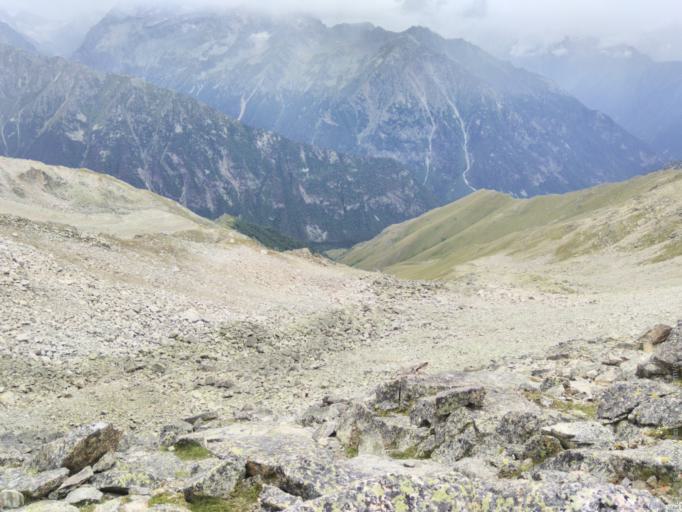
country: RU
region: Karachayevo-Cherkesiya
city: Uchkulan
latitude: 43.3468
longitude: 42.2975
